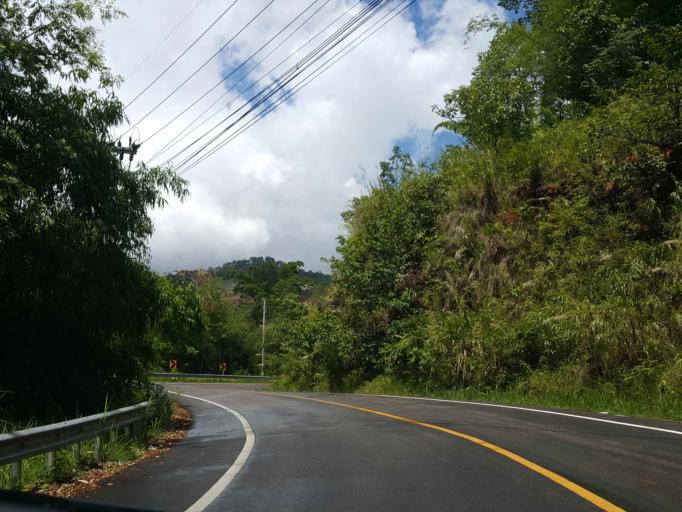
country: TH
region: Chiang Mai
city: Samoeng
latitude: 18.8541
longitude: 98.7720
